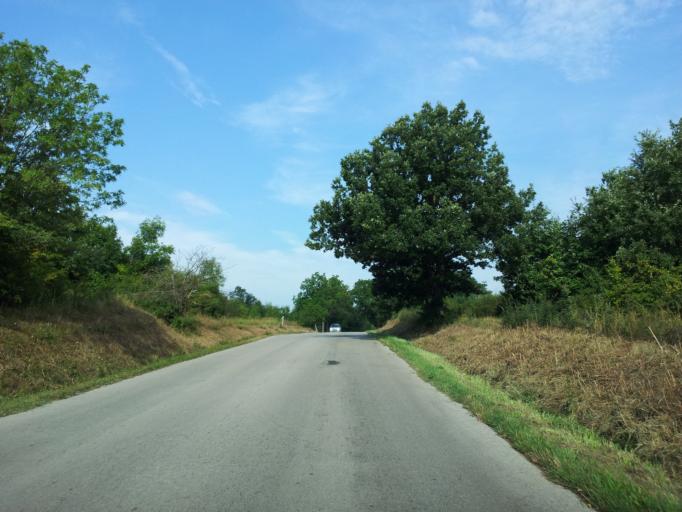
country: HU
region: Veszprem
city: Badacsonytomaj
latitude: 46.8533
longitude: 17.5461
